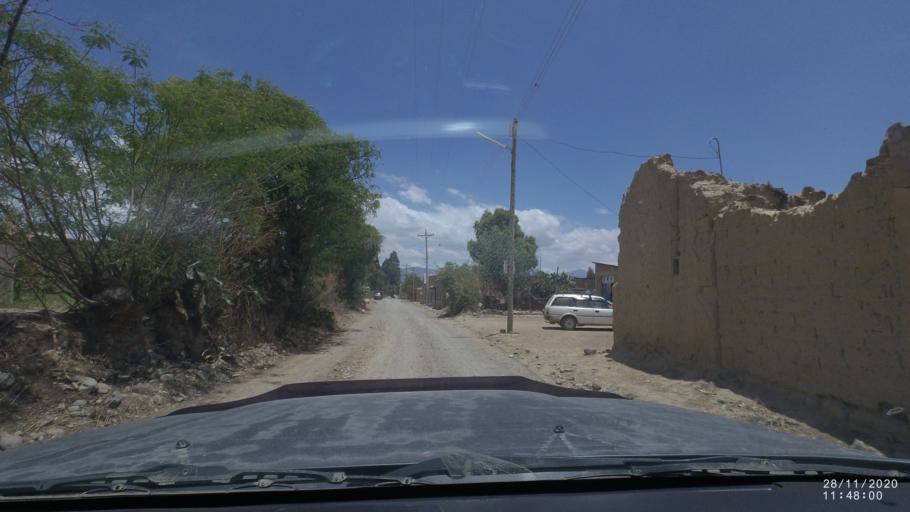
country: BO
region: Cochabamba
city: Tarata
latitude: -17.6417
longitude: -66.0332
